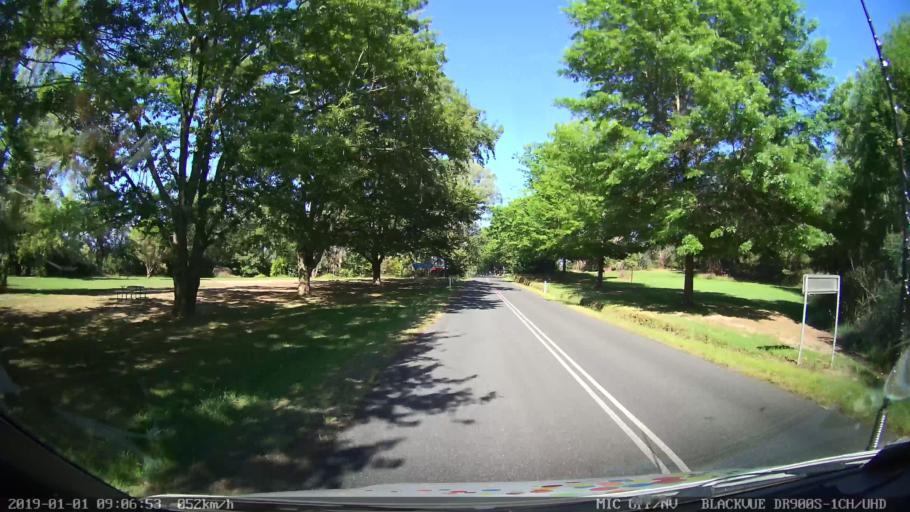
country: AU
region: New South Wales
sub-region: Snowy River
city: Jindabyne
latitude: -36.2174
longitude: 148.1334
